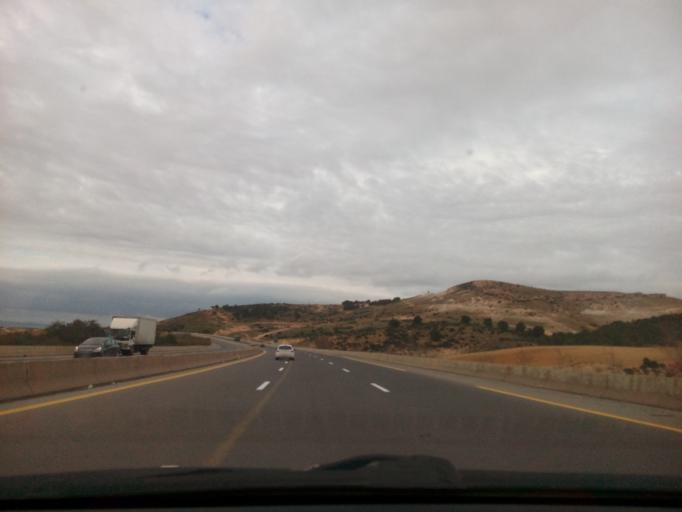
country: DZ
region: Sidi Bel Abbes
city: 'Ain el Berd
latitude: 35.4640
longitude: -0.3831
